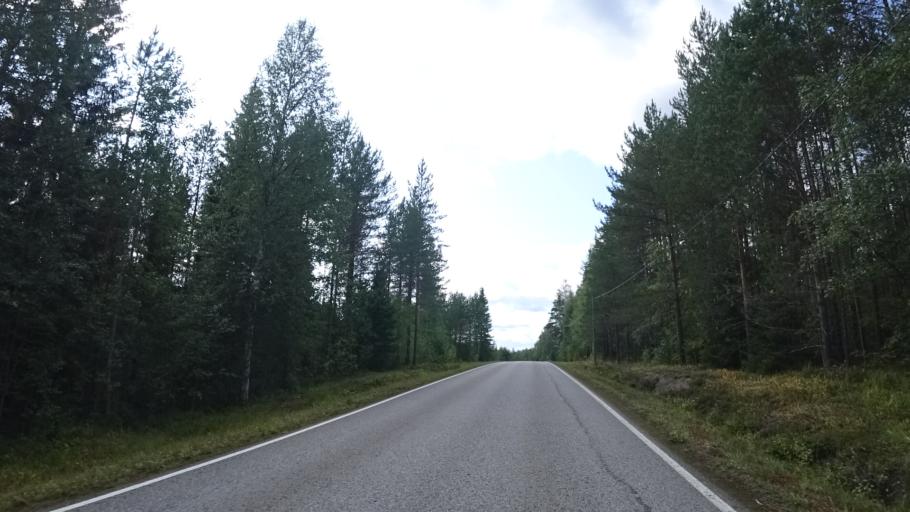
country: RU
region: Republic of Karelia
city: Vyartsilya
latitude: 62.2570
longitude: 30.7588
